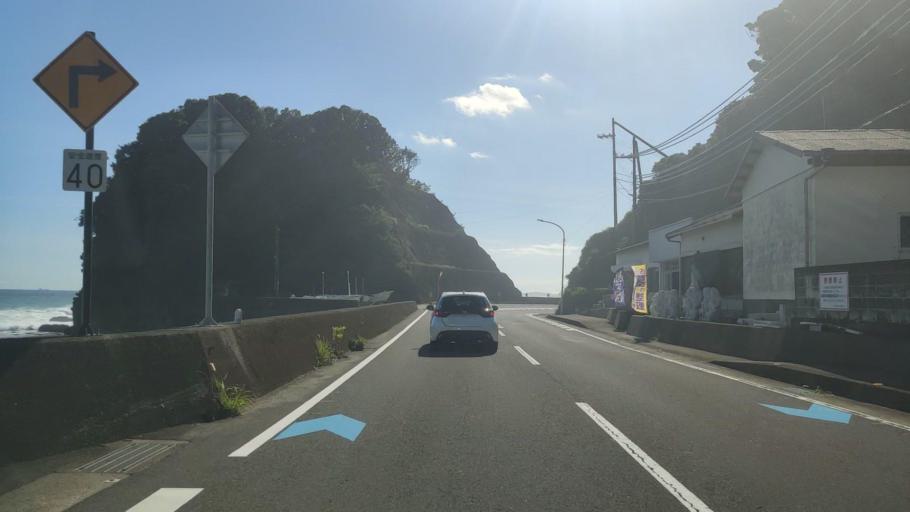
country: JP
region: Wakayama
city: Tanabe
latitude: 33.5035
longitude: 135.6411
